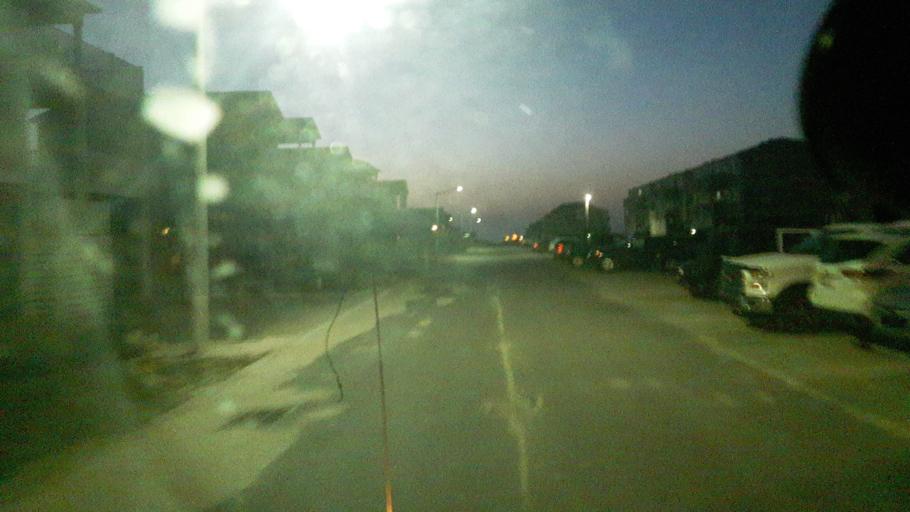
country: US
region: North Carolina
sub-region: Brunswick County
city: Shallotte
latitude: 33.8981
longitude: -78.3962
